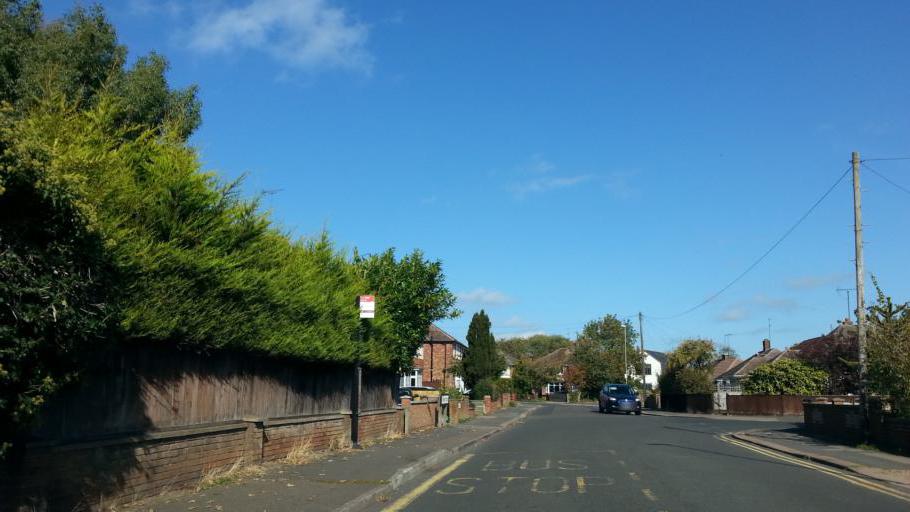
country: GB
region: England
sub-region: Northamptonshire
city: Rushden
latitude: 52.2818
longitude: -0.6003
